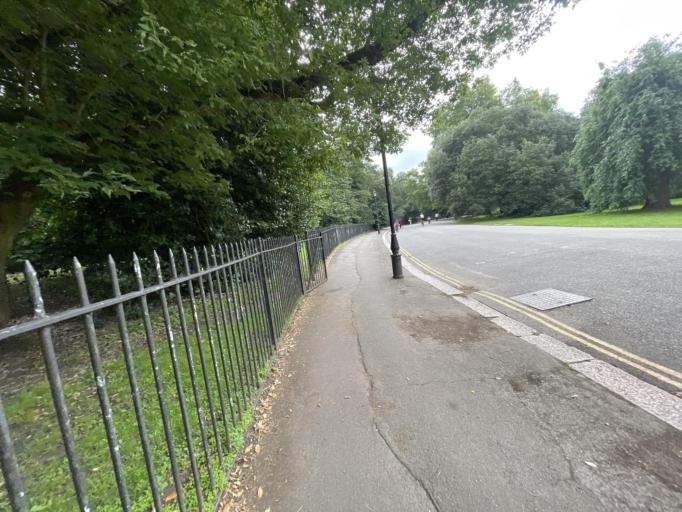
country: GB
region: England
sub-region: Greater London
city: Battersea
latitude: 51.4796
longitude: -0.1500
